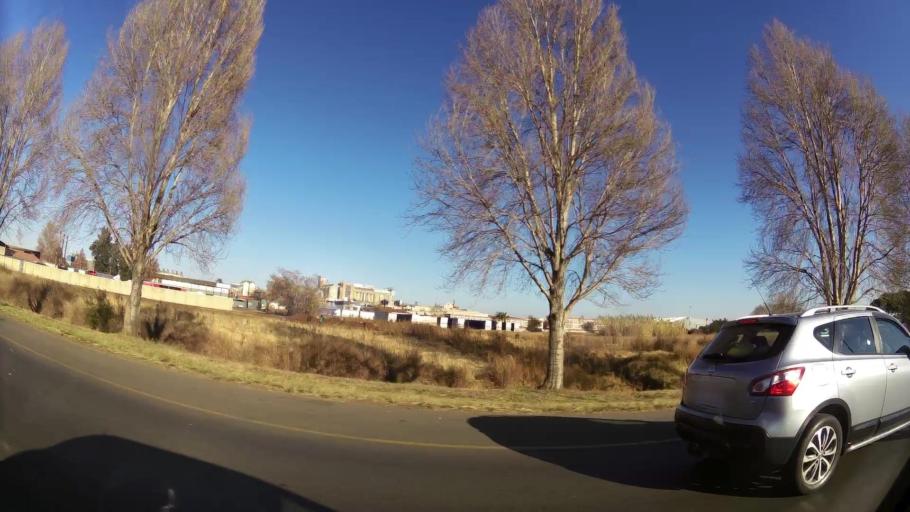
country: ZA
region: Gauteng
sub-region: Ekurhuleni Metropolitan Municipality
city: Germiston
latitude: -26.3093
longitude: 28.1387
